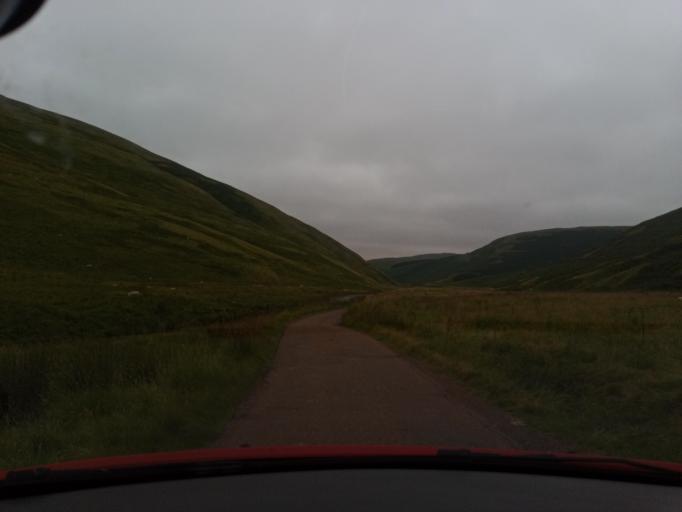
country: GB
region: England
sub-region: Northumberland
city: Rochester
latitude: 55.3851
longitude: -2.2128
